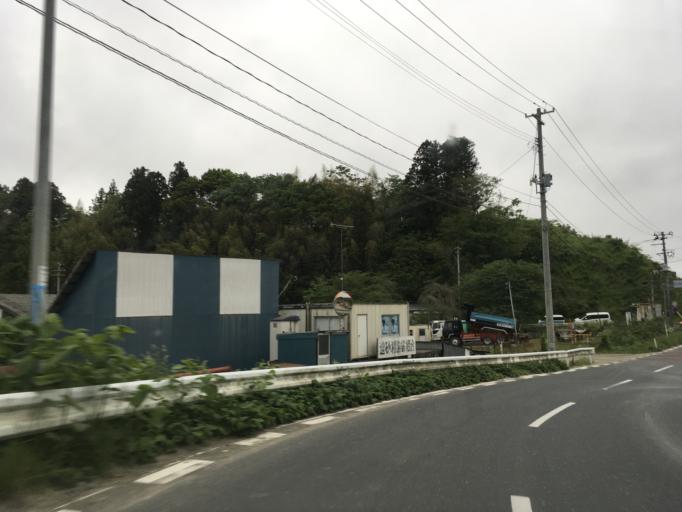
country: JP
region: Miyagi
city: Wakuya
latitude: 38.7144
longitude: 141.2944
